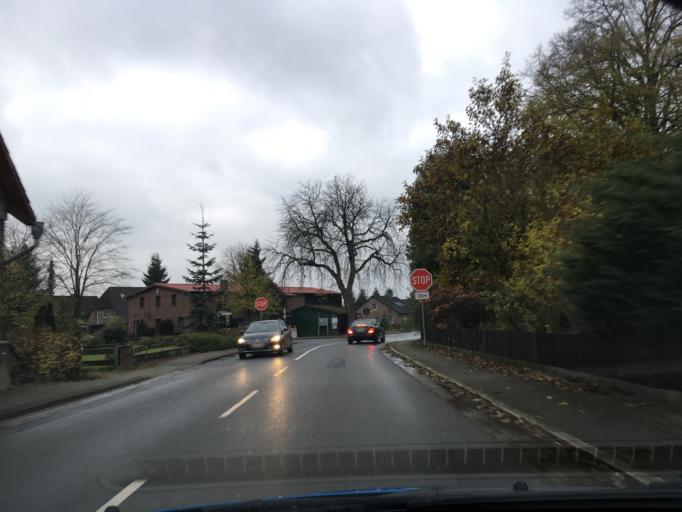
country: DE
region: Lower Saxony
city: Egestorf
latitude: 53.1515
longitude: 10.0678
